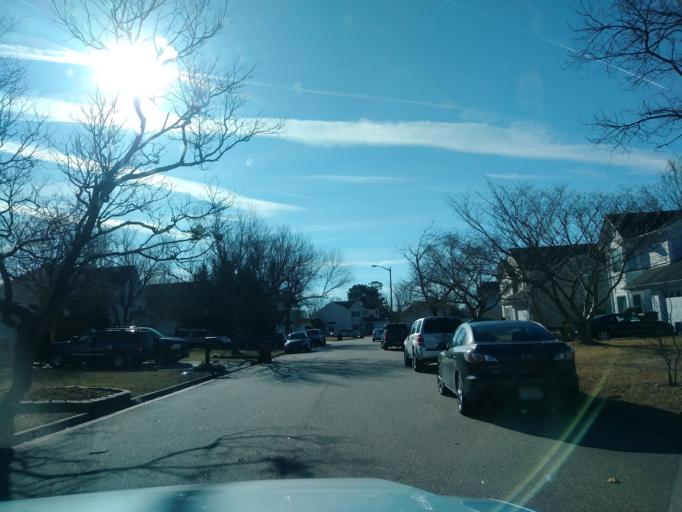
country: US
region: Virginia
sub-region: City of Chesapeake
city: Chesapeake
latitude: 36.7543
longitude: -76.2089
